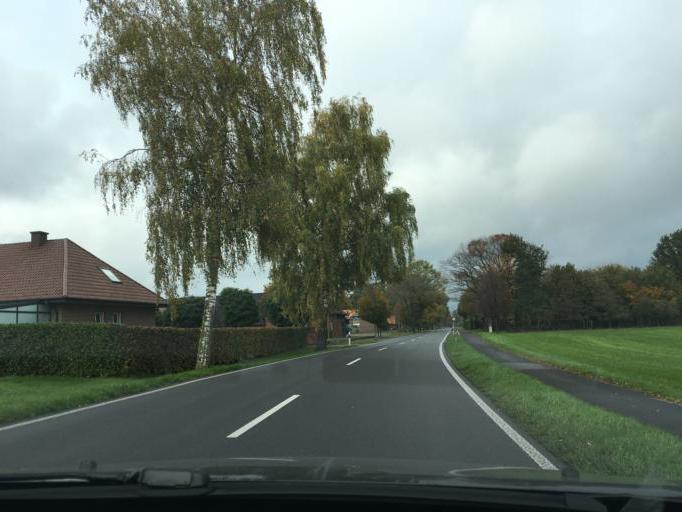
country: DE
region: North Rhine-Westphalia
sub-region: Regierungsbezirk Munster
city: Vreden
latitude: 52.0605
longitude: 6.7974
